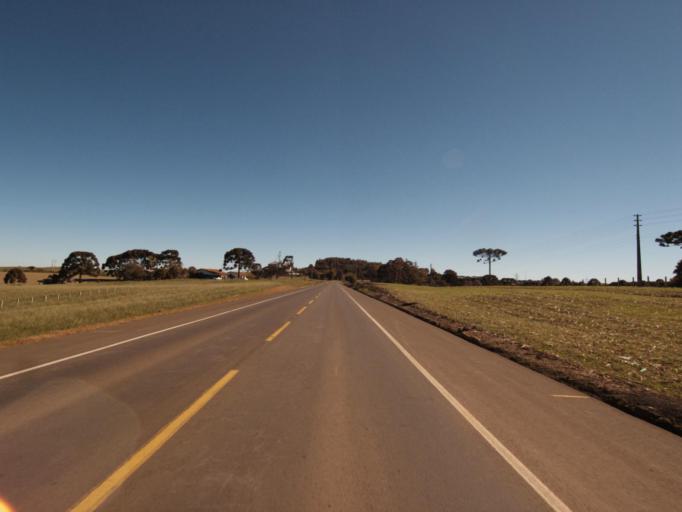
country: BR
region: Santa Catarina
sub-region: Xanxere
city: Xanxere
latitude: -26.8617
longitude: -52.2332
